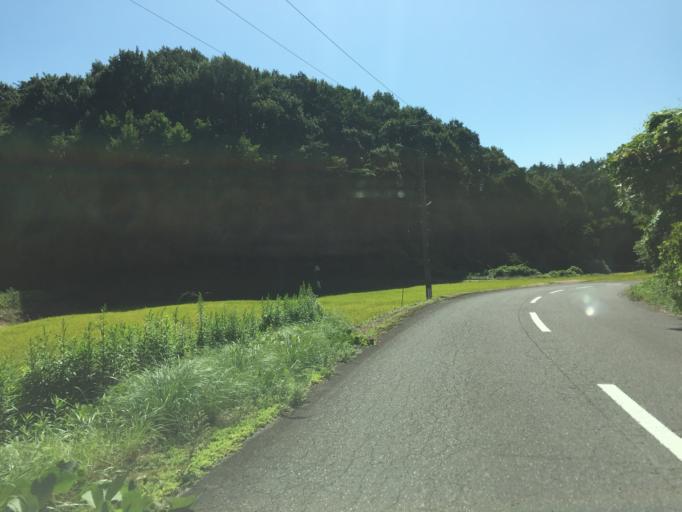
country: JP
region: Fukushima
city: Sukagawa
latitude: 37.2799
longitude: 140.4719
